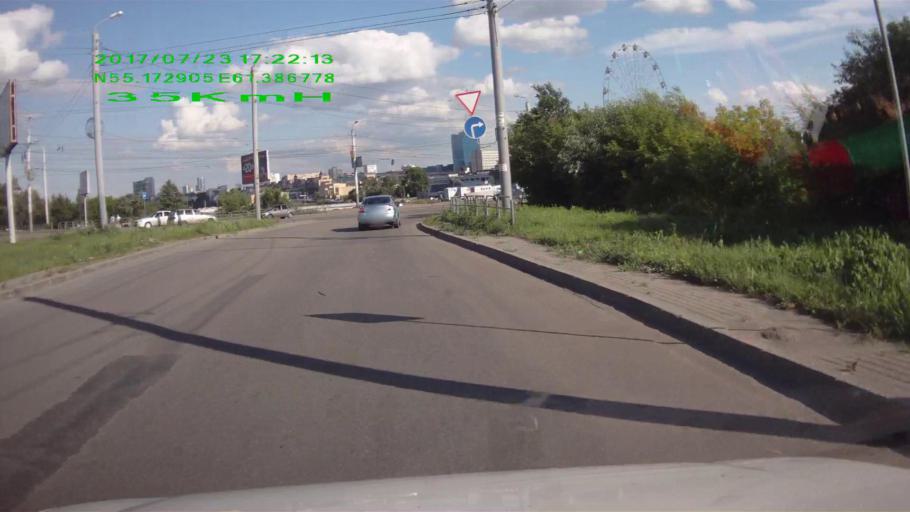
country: RU
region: Chelyabinsk
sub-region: Gorod Chelyabinsk
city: Chelyabinsk
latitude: 55.1727
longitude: 61.3874
